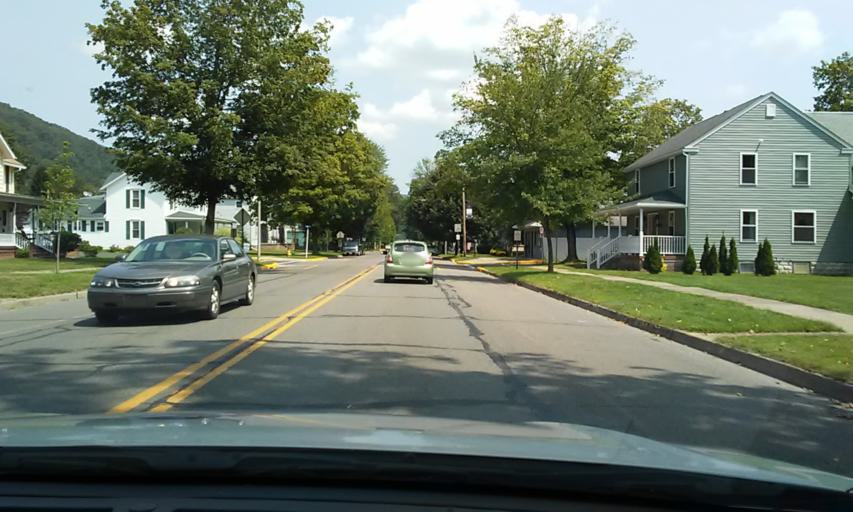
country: US
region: Pennsylvania
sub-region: Cameron County
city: Emporium
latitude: 41.5111
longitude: -78.2446
